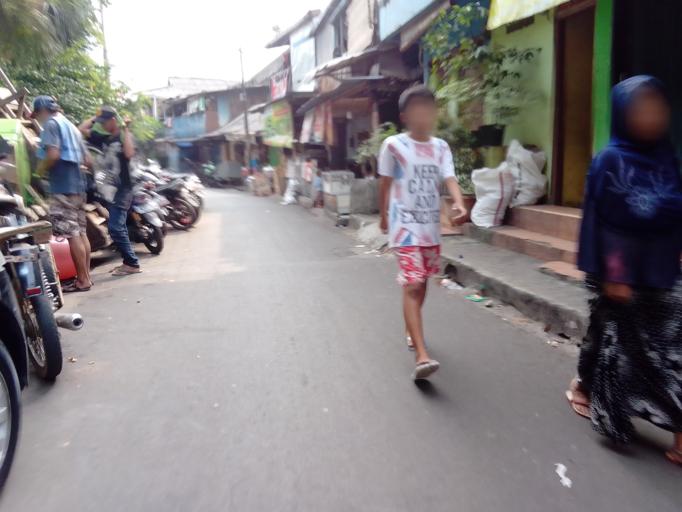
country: ID
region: Jakarta Raya
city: Jakarta
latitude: -6.1974
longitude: 106.8088
